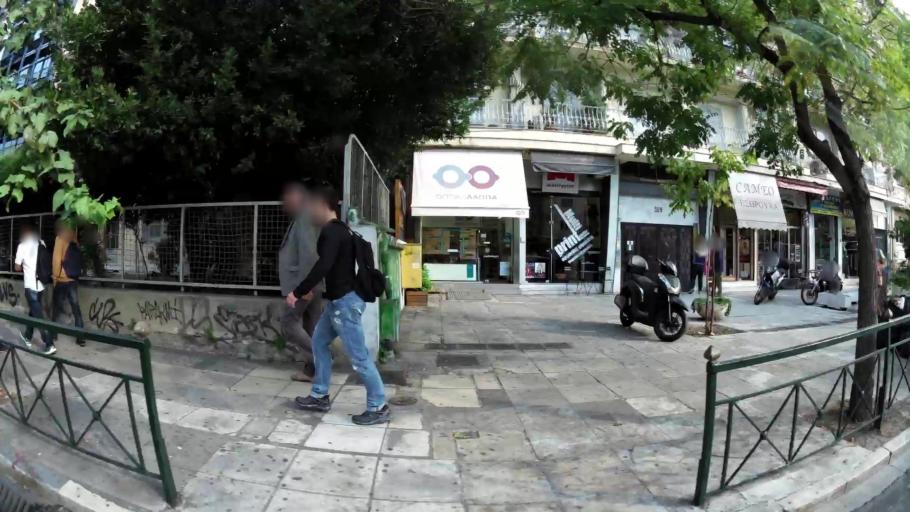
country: GR
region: Attica
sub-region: Nomarchia Athinas
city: Kaisariani
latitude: 37.9872
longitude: 23.7586
